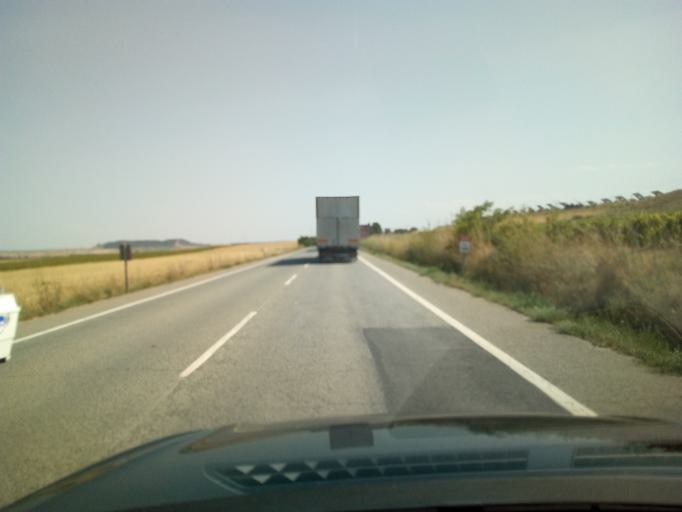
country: ES
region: Navarre
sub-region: Provincia de Navarra
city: Pitillas
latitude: 42.4371
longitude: -1.6469
